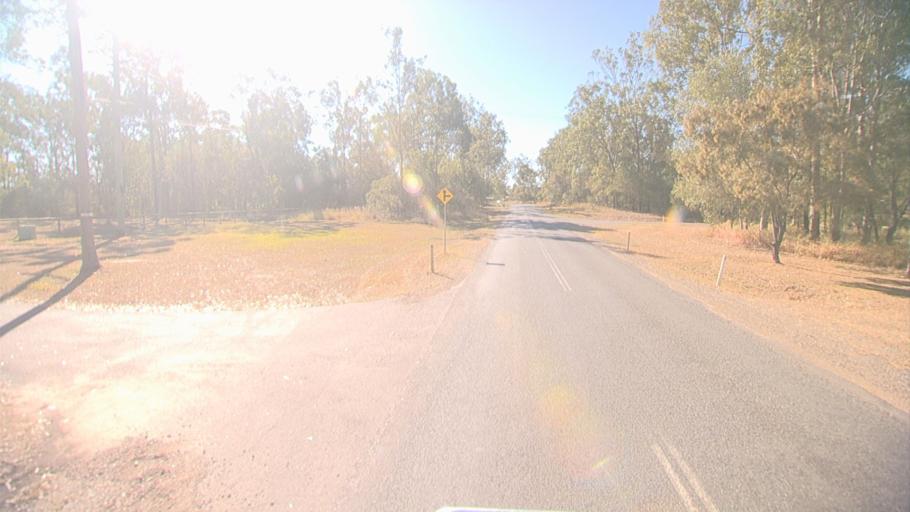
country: AU
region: Queensland
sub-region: Logan
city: North Maclean
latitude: -27.7560
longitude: 152.9957
